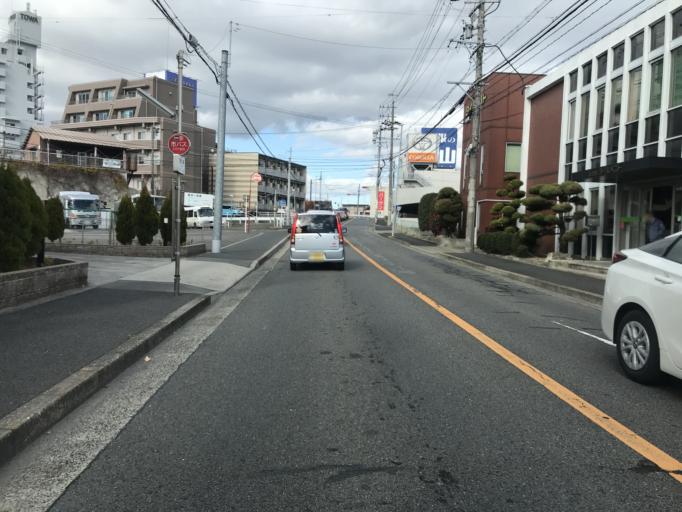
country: JP
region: Aichi
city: Nagoya-shi
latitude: 35.1766
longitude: 136.8493
